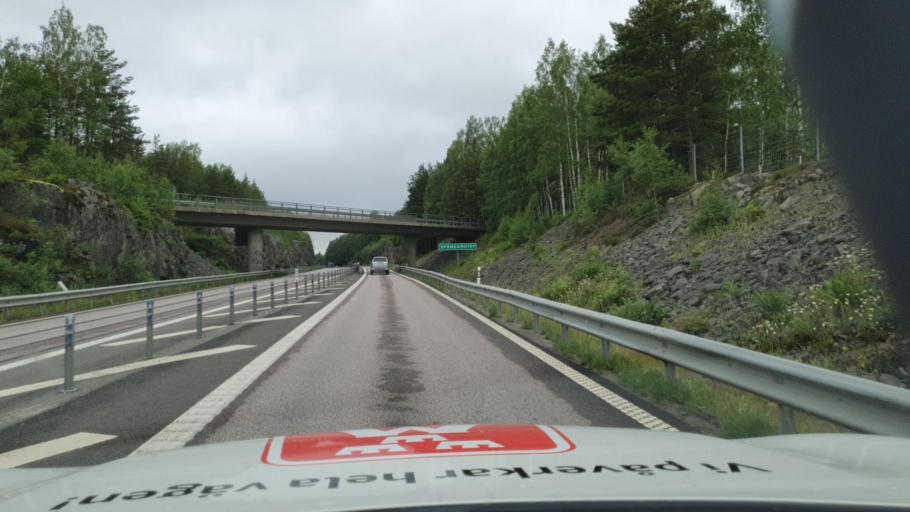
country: SE
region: Vaermland
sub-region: Karlstads Kommun
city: Skattkarr
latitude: 59.4162
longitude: 13.7393
